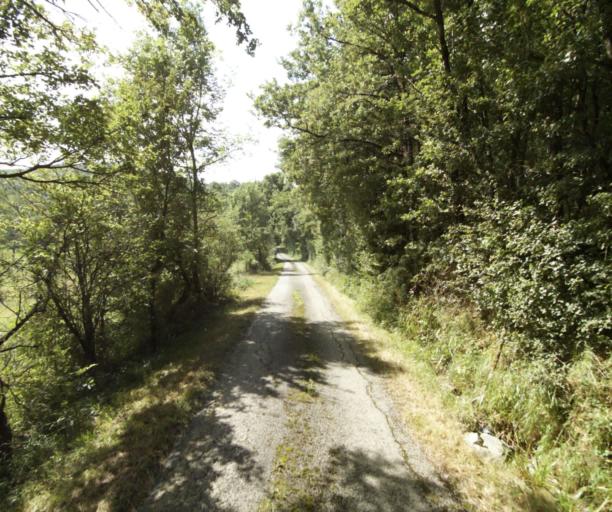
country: FR
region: Midi-Pyrenees
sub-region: Departement du Tarn
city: Dourgne
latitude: 43.4696
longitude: 2.1152
